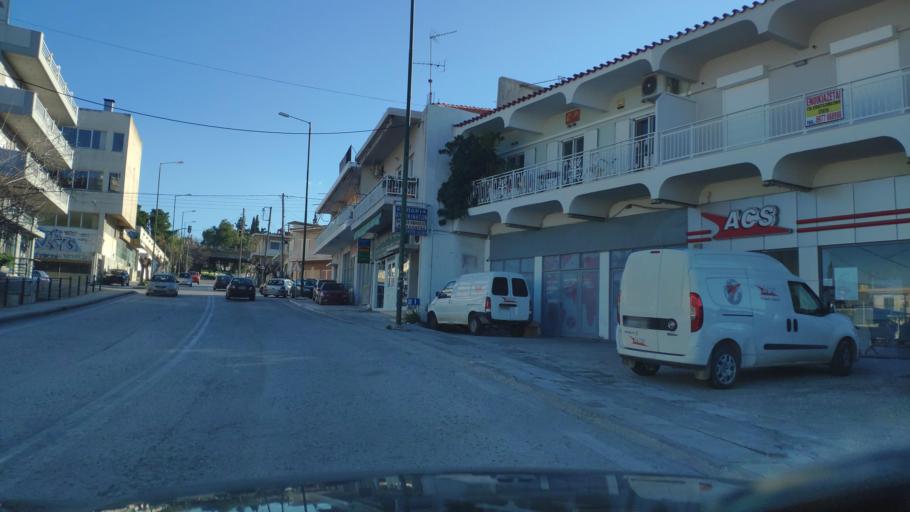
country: GR
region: Peloponnese
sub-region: Nomos Korinthias
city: Korinthos
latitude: 37.9337
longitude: 22.9271
